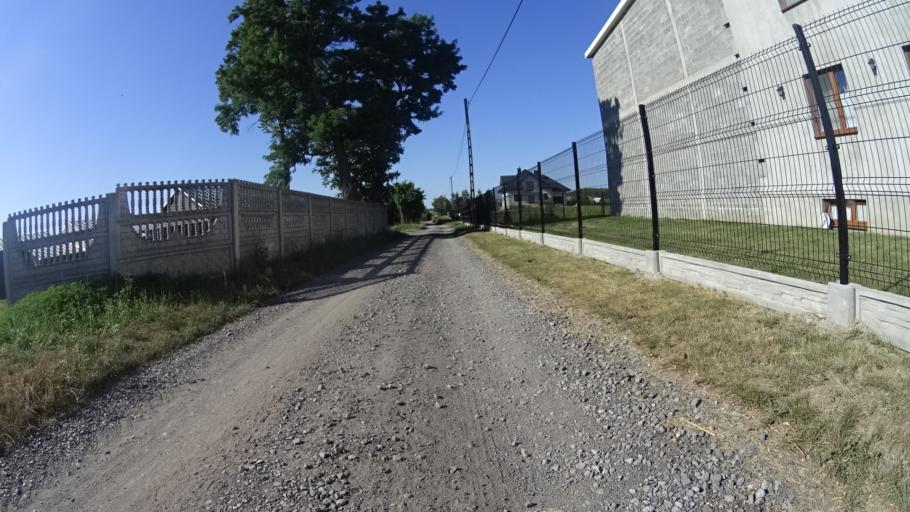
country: PL
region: Masovian Voivodeship
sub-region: Powiat bialobrzeski
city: Wysmierzyce
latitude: 51.6652
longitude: 20.8497
